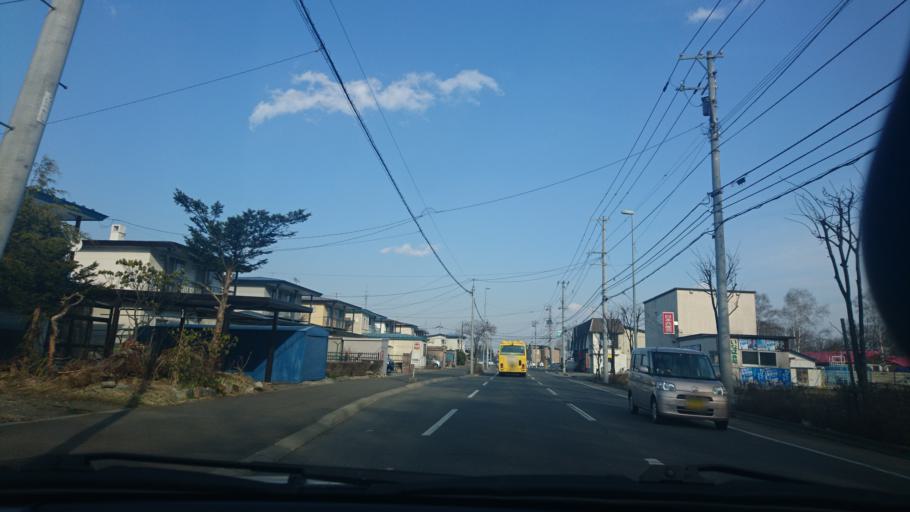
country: JP
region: Hokkaido
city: Obihiro
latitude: 42.9241
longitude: 143.1756
